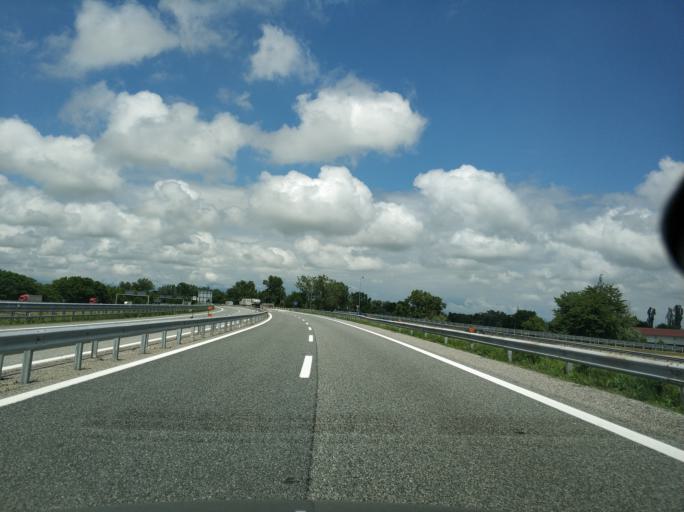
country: IT
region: Piedmont
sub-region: Provincia di Torino
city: Settimo Torinese
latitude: 45.1331
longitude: 7.7290
